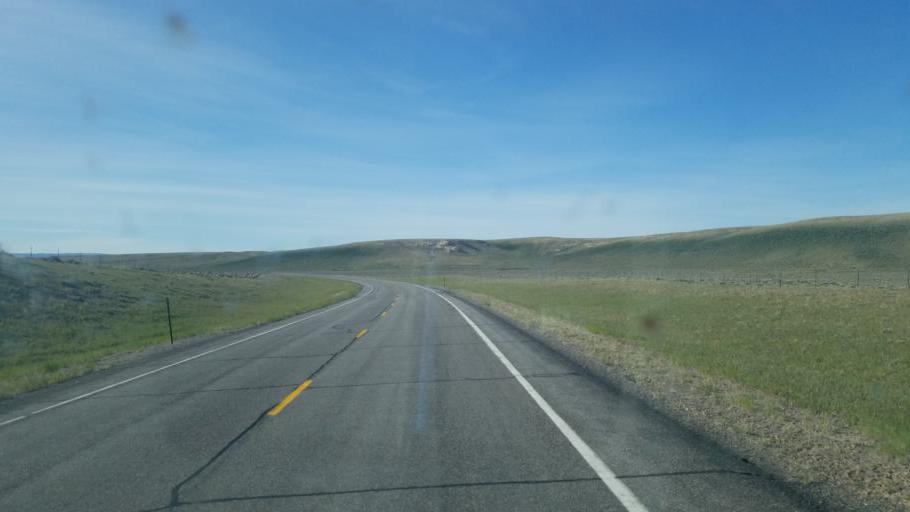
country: US
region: Wyoming
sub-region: Fremont County
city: Riverton
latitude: 42.6213
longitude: -108.1951
